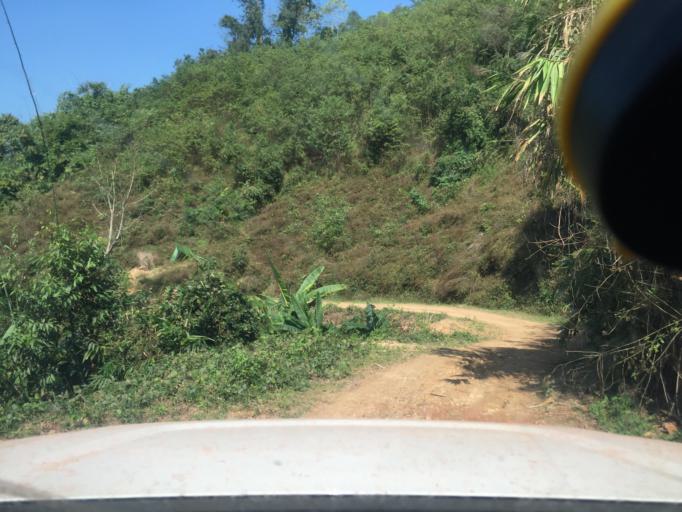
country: LA
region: Phongsali
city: Phongsali
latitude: 21.6486
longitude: 102.4088
